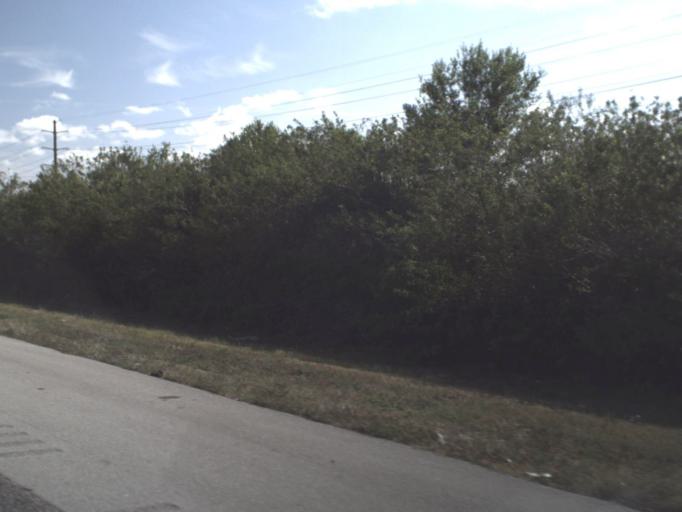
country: US
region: Florida
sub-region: Brevard County
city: June Park
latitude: 28.0934
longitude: -80.7062
